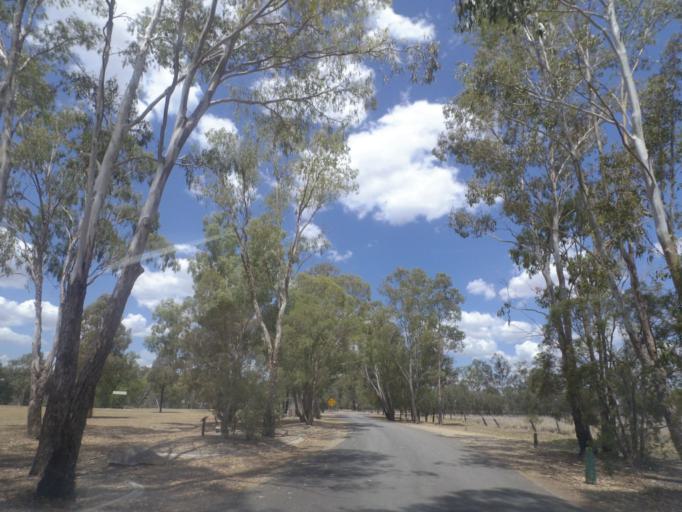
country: AU
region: Queensland
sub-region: Southern Downs
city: Warwick
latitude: -28.2106
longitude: 152.0377
